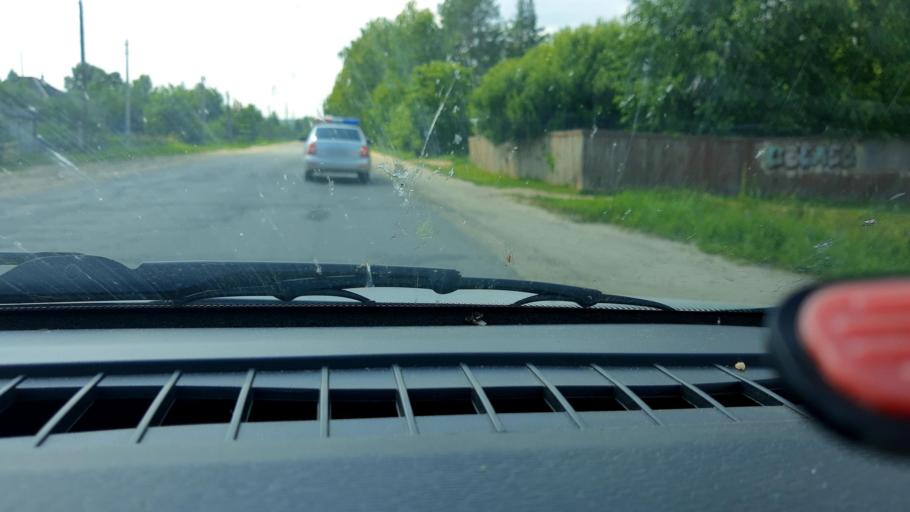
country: RU
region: Nizjnij Novgorod
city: Uren'
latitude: 57.4857
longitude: 45.9673
